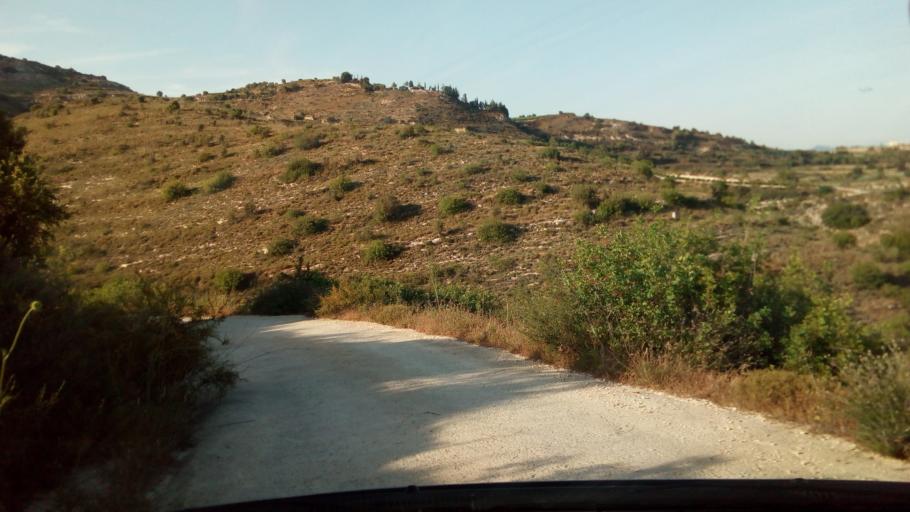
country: CY
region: Pafos
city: Tala
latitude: 34.8719
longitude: 32.4692
